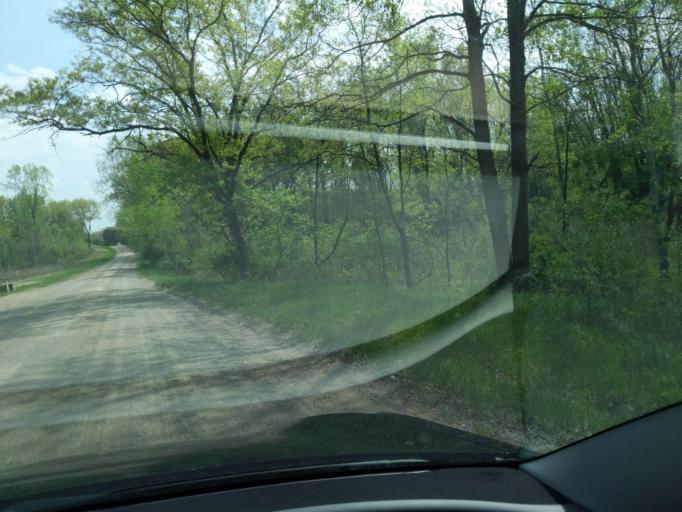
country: US
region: Michigan
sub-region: Ingham County
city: Stockbridge
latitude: 42.4349
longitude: -84.0761
